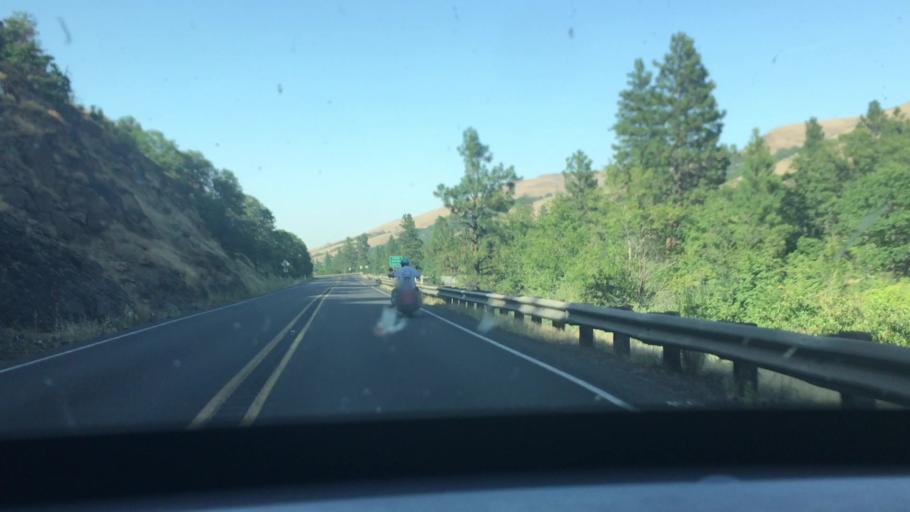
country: US
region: Washington
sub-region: Klickitat County
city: Goldendale
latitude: 46.0407
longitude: -120.5745
